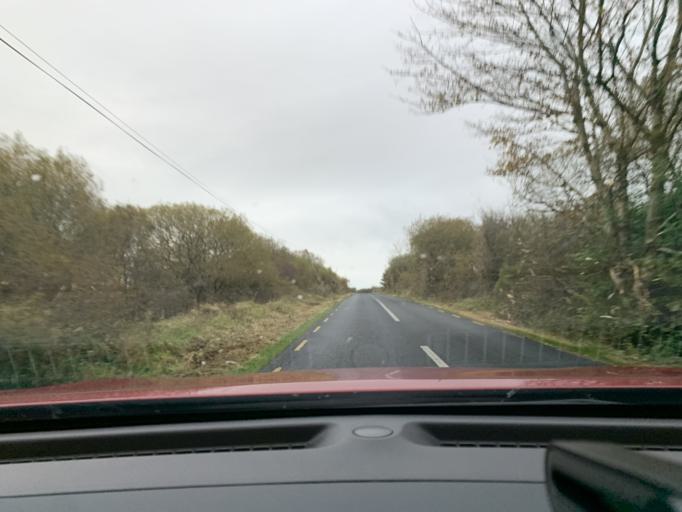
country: IE
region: Connaught
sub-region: Roscommon
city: Ballaghaderreen
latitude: 53.9532
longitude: -8.5441
